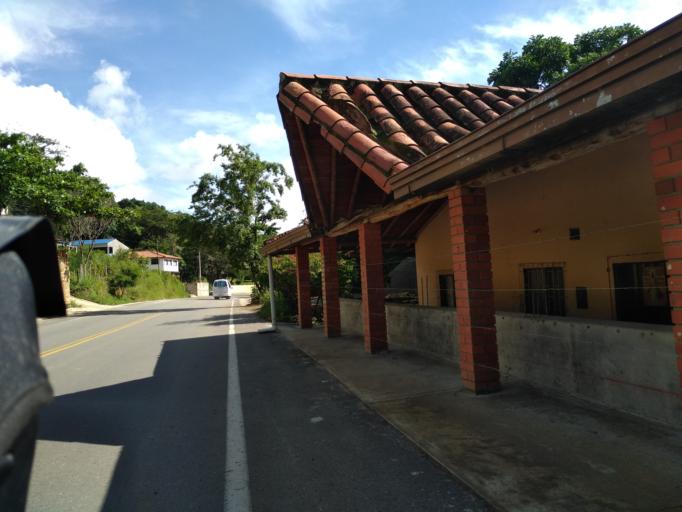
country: CO
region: Santander
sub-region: San Gil
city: San Gil
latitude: 6.5171
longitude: -73.1252
